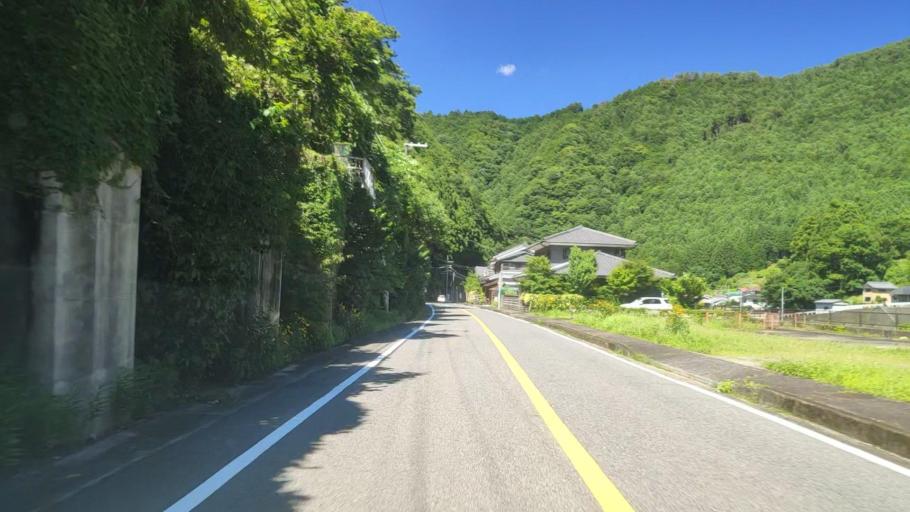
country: JP
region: Nara
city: Yoshino-cho
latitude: 34.2928
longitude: 135.9997
